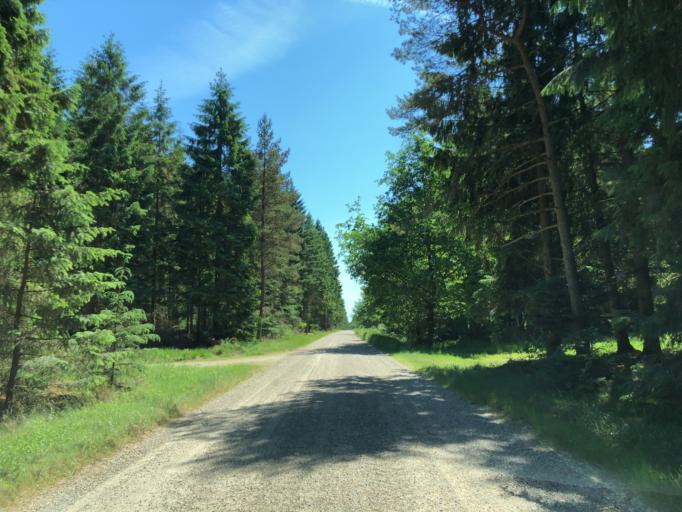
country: DK
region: Central Jutland
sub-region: Struer Kommune
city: Struer
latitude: 56.4393
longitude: 8.4397
